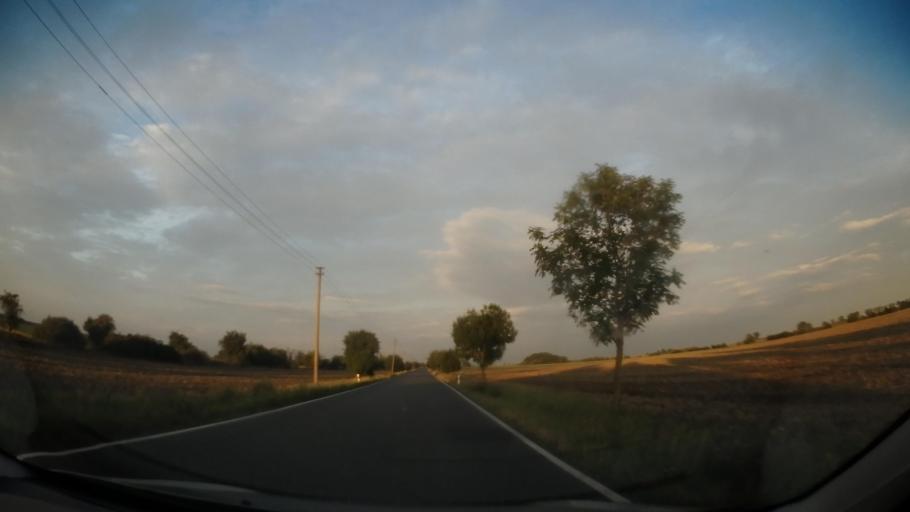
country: CZ
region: Central Bohemia
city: Loucen
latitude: 50.2355
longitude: 14.9768
